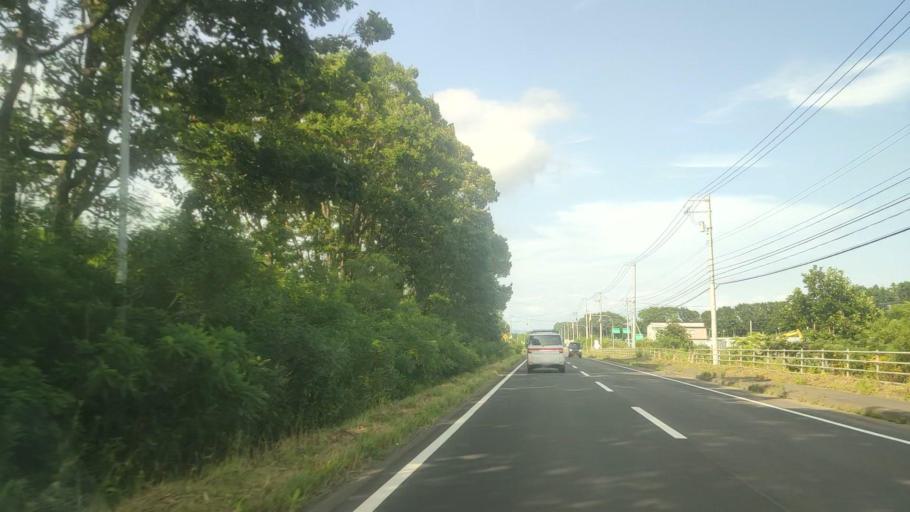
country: JP
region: Hokkaido
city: Chitose
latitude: 42.7424
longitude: 141.7859
